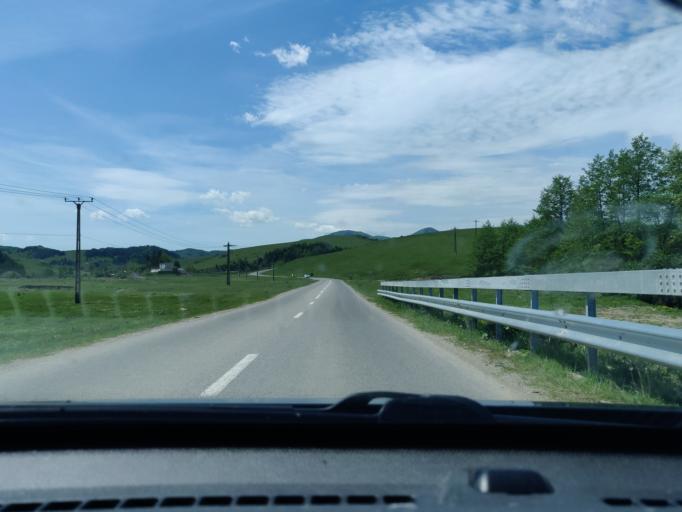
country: RO
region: Vrancea
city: Dragosloveni
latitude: 46.0102
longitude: 26.6816
